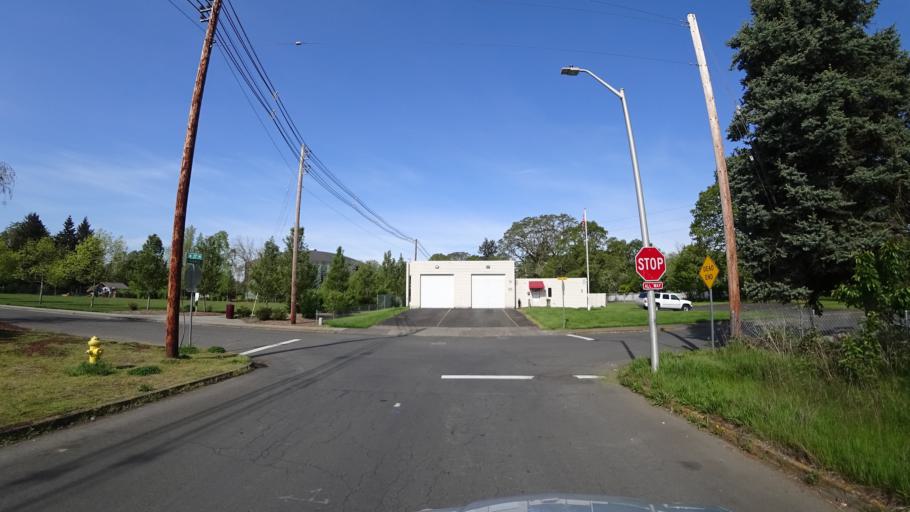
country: US
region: Oregon
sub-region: Washington County
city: Hillsboro
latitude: 45.5238
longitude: -122.9563
